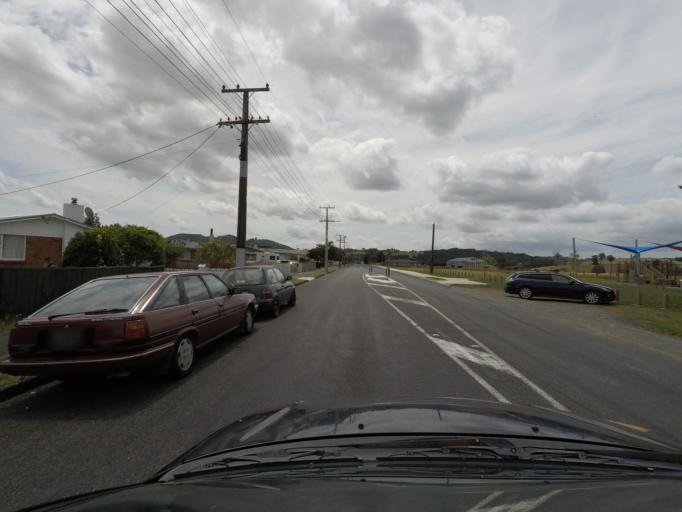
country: NZ
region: Northland
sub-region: Whangarei
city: Whangarei
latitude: -35.6816
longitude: 174.3253
